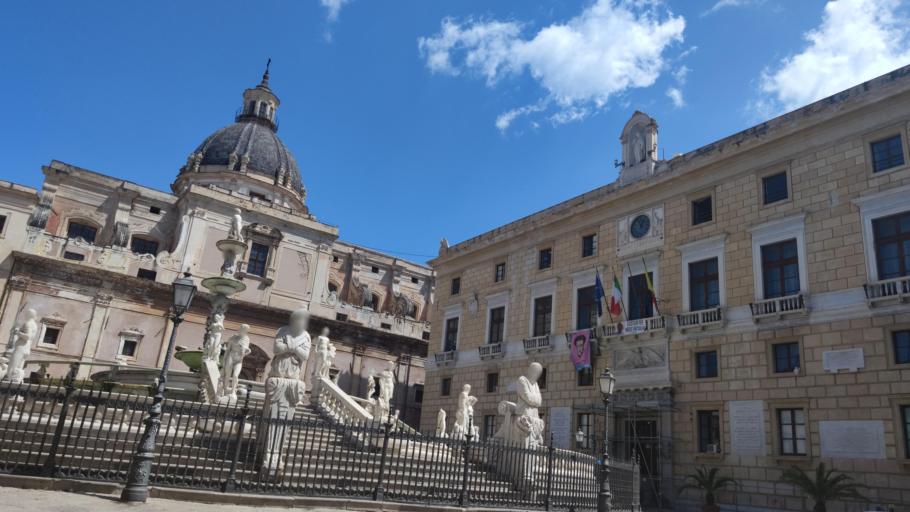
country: IT
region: Sicily
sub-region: Palermo
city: Palermo
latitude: 38.1155
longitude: 13.3617
